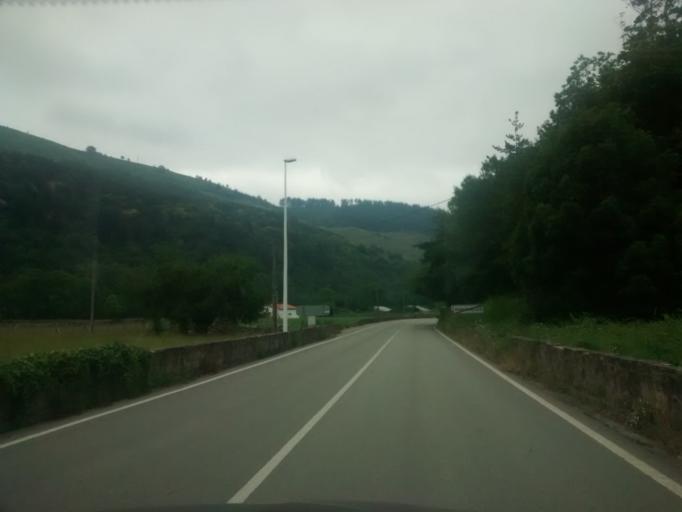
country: ES
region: Cantabria
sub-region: Provincia de Cantabria
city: Ruente
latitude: 43.2437
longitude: -4.2846
